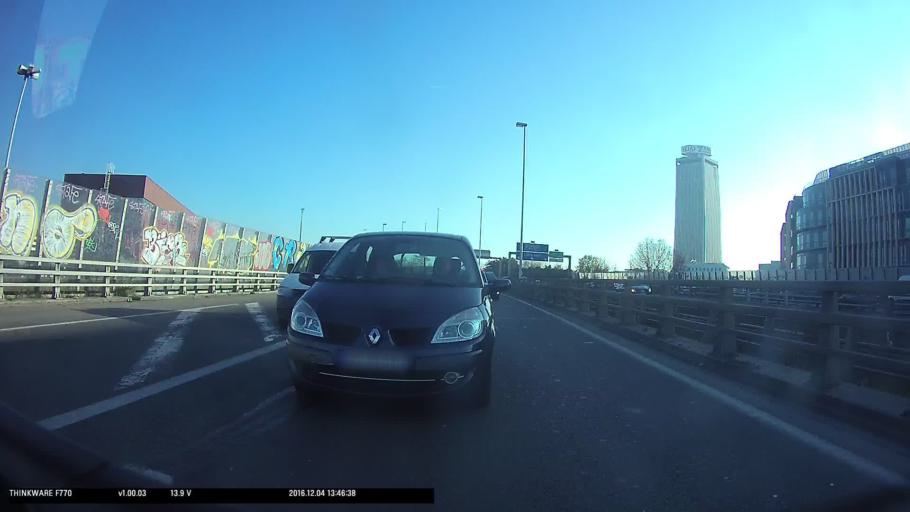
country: FR
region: Ile-de-France
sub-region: Paris
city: Saint-Ouen
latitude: 48.9240
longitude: 2.3425
